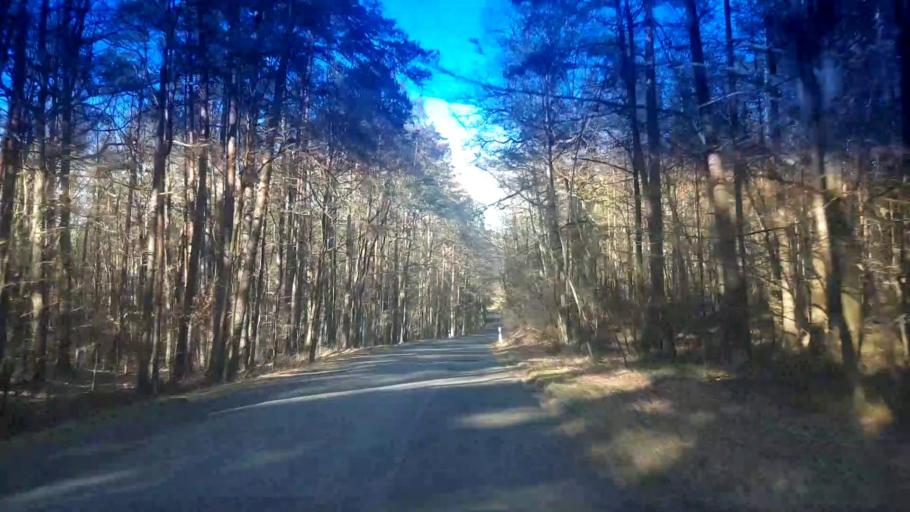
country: DE
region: Bavaria
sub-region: Upper Franconia
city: Lauter
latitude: 49.9621
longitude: 10.7620
